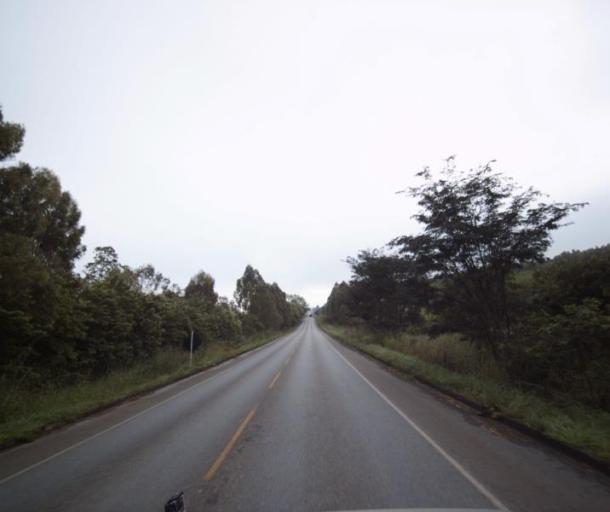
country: BR
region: Goias
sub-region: Pirenopolis
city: Pirenopolis
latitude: -15.8043
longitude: -48.7804
